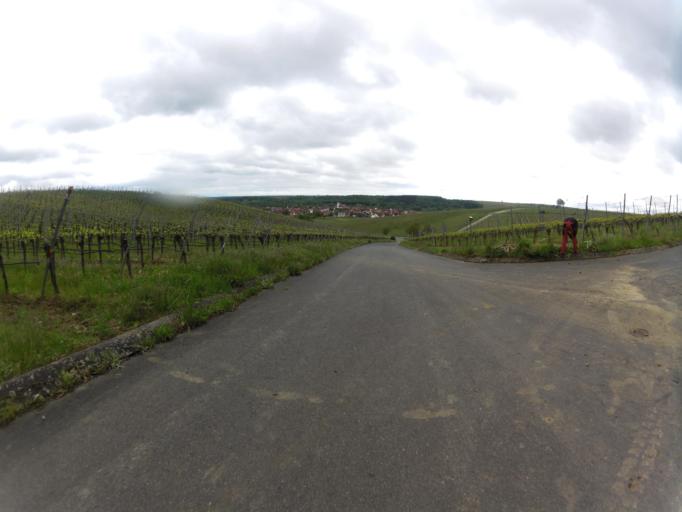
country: DE
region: Bavaria
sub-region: Regierungsbezirk Unterfranken
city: Sommerach
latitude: 49.8386
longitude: 10.2092
